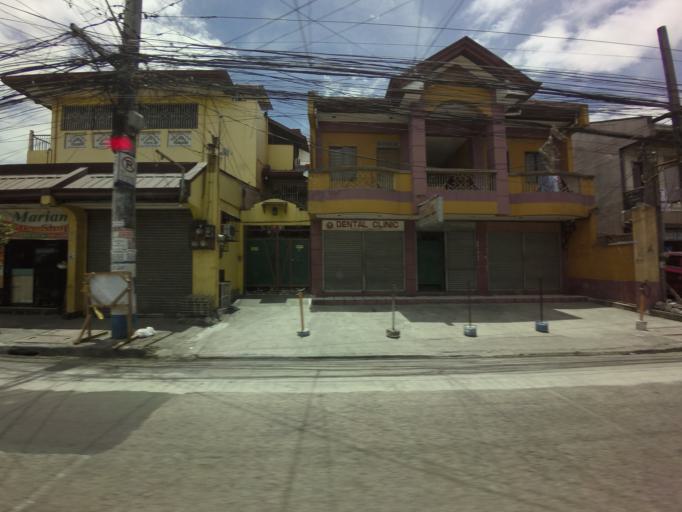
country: PH
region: Calabarzon
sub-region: Province of Rizal
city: Cainta
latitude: 14.5881
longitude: 121.0973
